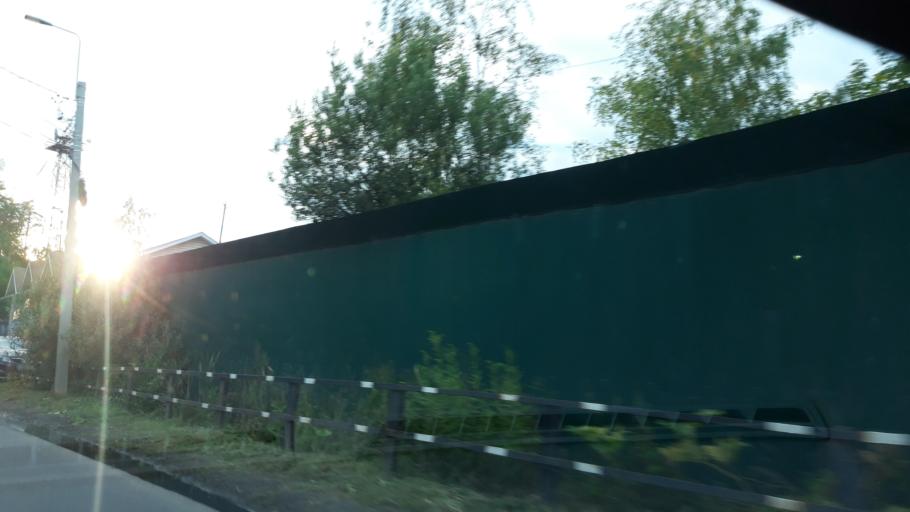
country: RU
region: Moskovskaya
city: Andreyevka
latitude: 55.9828
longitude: 37.1133
